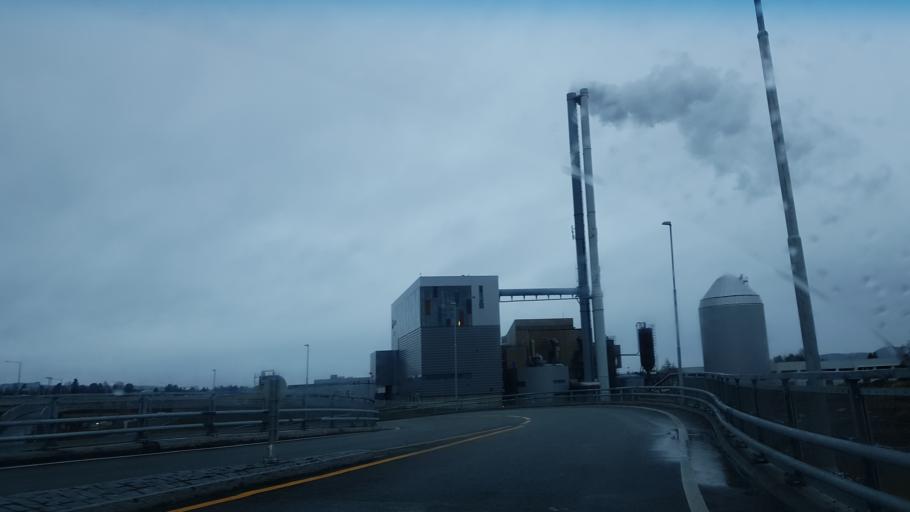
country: NO
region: Sor-Trondelag
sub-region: Trondheim
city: Trondheim
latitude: 63.3465
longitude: 10.3715
